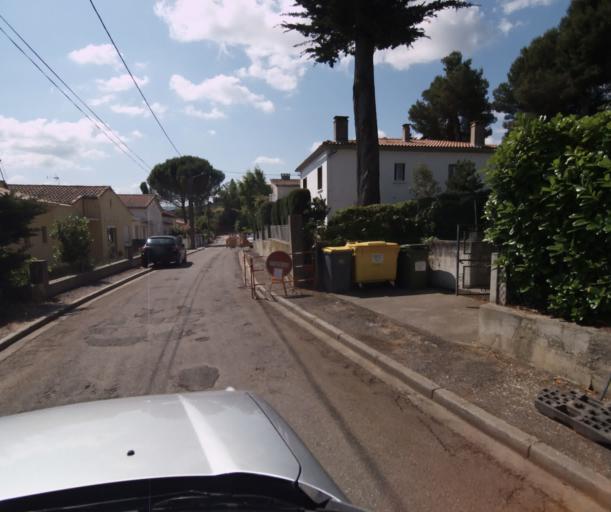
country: FR
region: Languedoc-Roussillon
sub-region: Departement de l'Aude
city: Limoux
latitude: 43.0528
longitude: 2.2132
